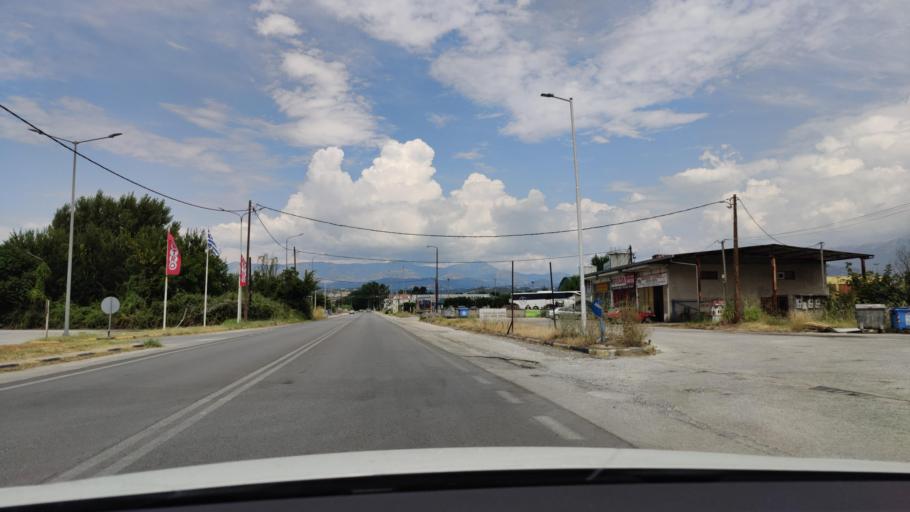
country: GR
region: Central Macedonia
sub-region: Nomos Serron
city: Serres
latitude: 41.0645
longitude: 23.5403
